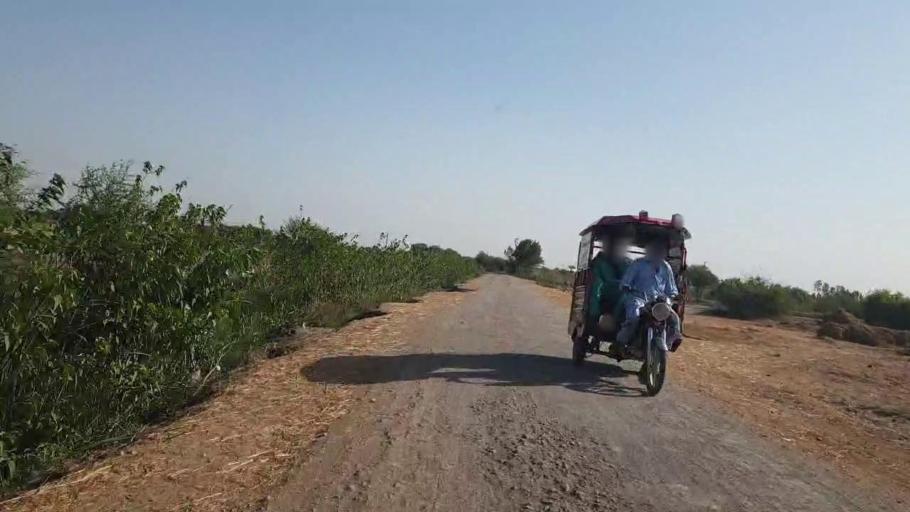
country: PK
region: Sindh
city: Matli
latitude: 25.0372
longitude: 68.7287
